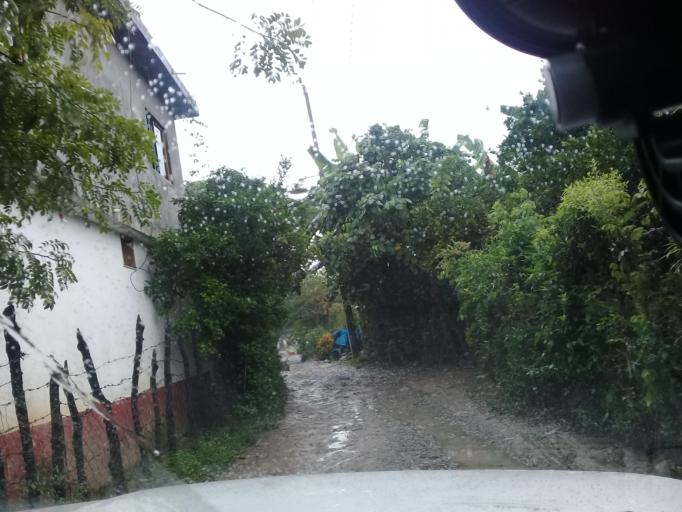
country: MX
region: Veracruz
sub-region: Chalma
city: San Pedro Coyutla
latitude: 21.1840
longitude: -98.4346
